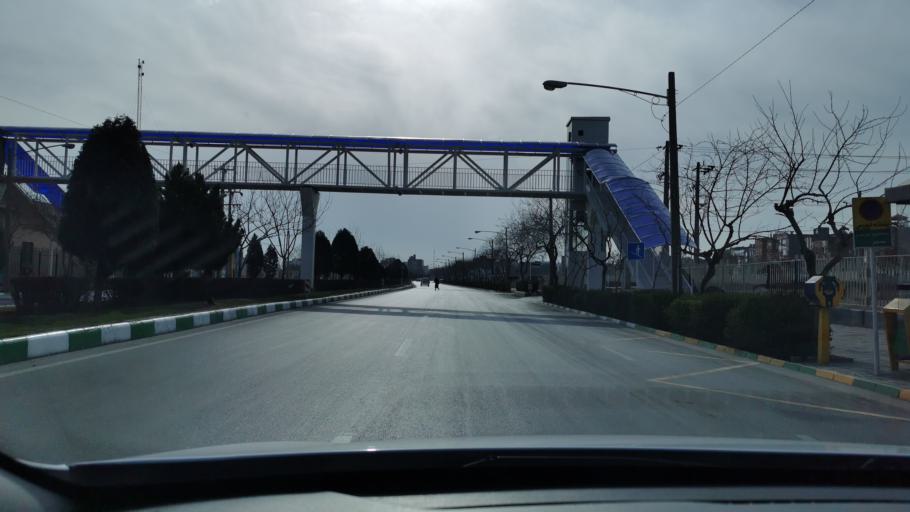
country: IR
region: Razavi Khorasan
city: Mashhad
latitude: 36.3014
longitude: 59.5192
